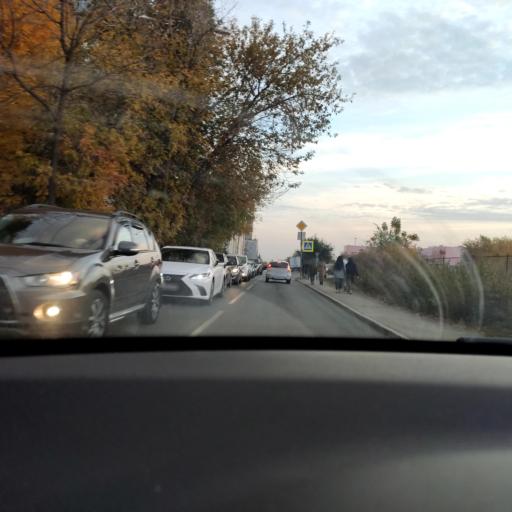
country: RU
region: Samara
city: Samara
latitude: 53.2108
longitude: 50.2028
